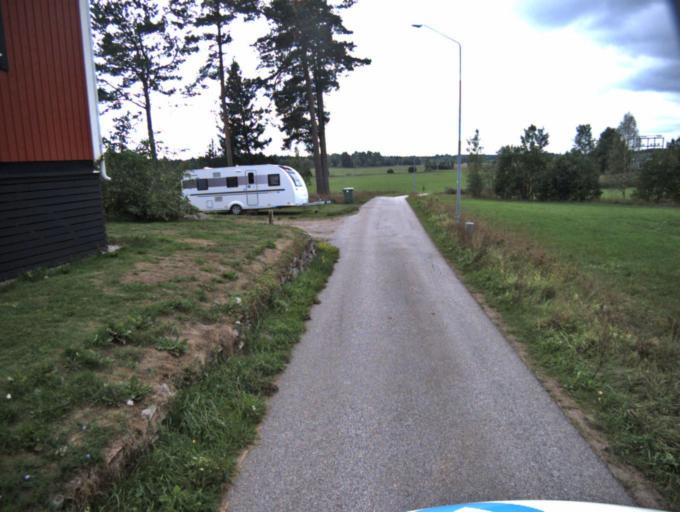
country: SE
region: Vaestra Goetaland
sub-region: Ulricehamns Kommun
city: Ulricehamn
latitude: 57.8987
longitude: 13.3485
